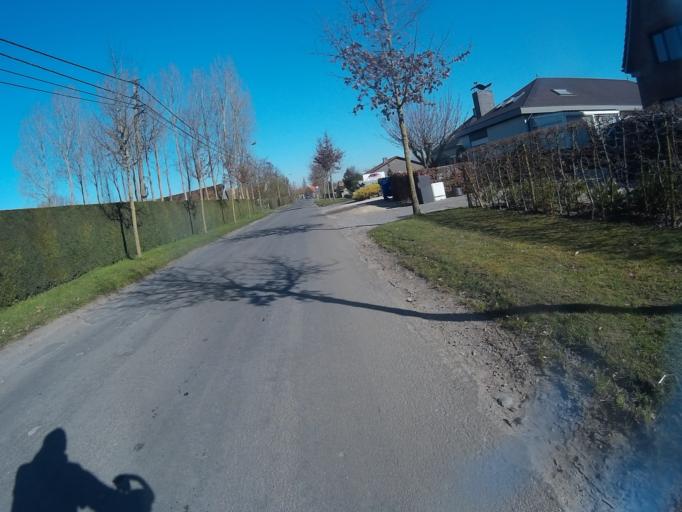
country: BE
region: Flanders
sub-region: Provincie Oost-Vlaanderen
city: Zomergem
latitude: 51.1228
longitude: 3.5036
